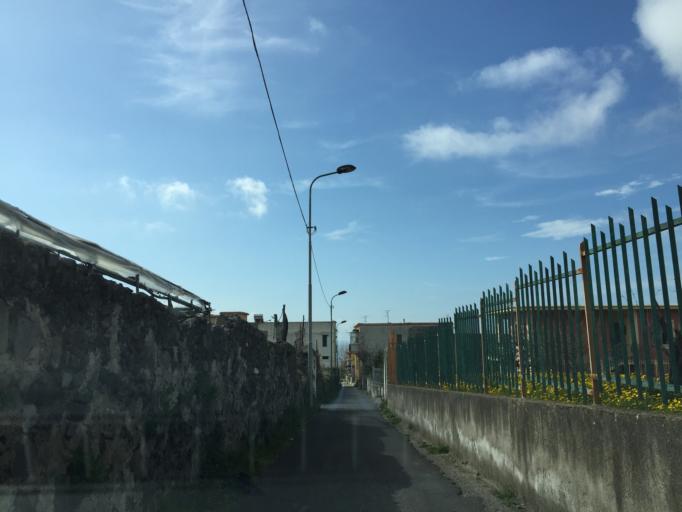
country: IT
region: Campania
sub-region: Provincia di Napoli
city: Torre del Greco
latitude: 40.7789
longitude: 14.4143
